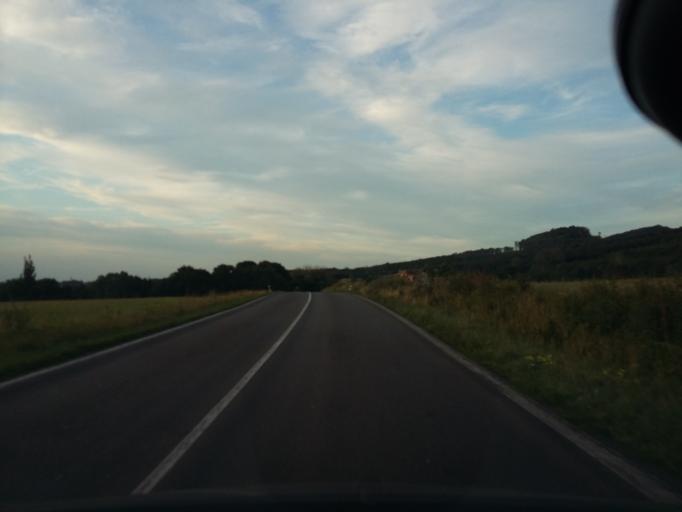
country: SK
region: Bratislavsky
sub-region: Okres Malacky
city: Malacky
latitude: 48.3807
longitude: 17.1514
